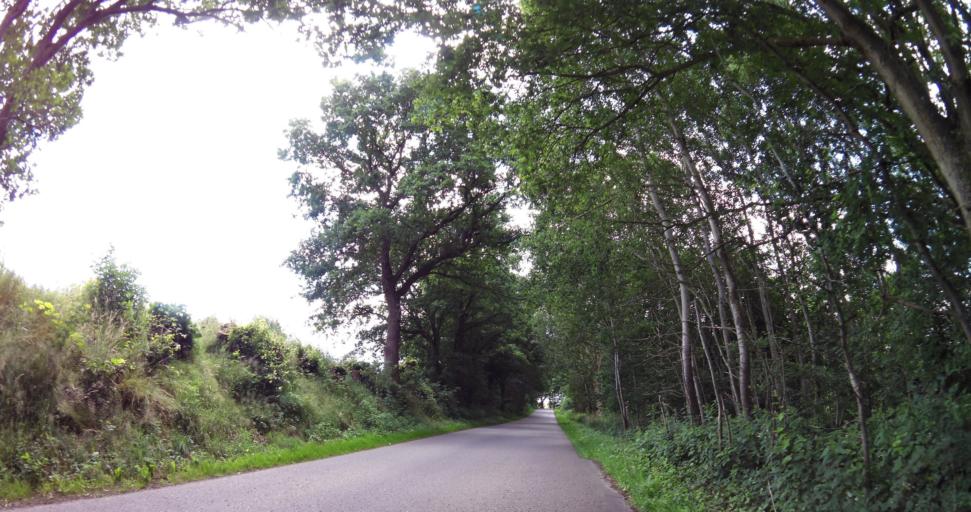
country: DE
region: Schleswig-Holstein
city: Fleckeby
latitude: 54.4968
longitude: 9.7296
